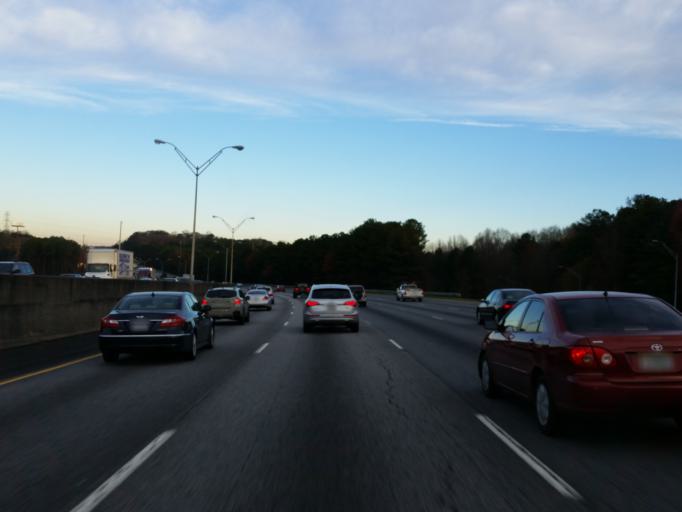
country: US
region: Georgia
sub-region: Cobb County
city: Marietta
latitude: 33.9577
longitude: -84.5167
